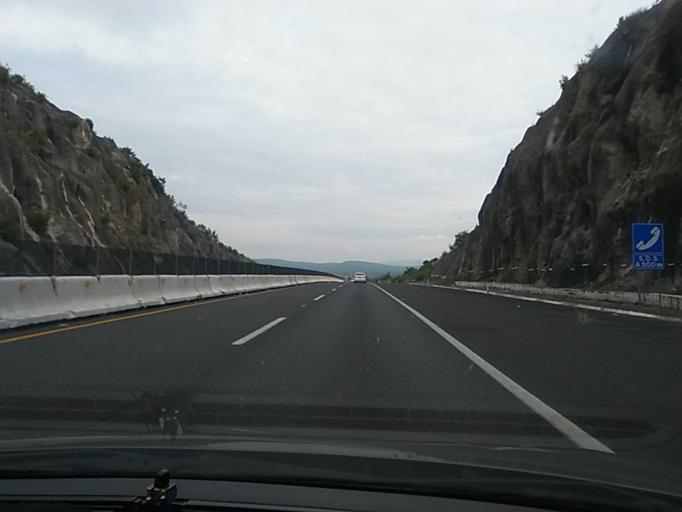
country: MX
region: Michoacan
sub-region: Puruandiro
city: San Lorenzo
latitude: 19.9414
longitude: -101.6276
